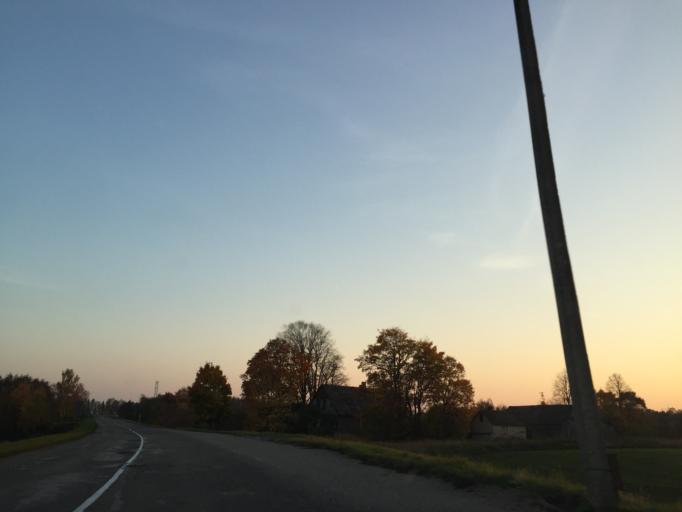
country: LT
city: Skuodas
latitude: 56.2984
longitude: 21.5387
